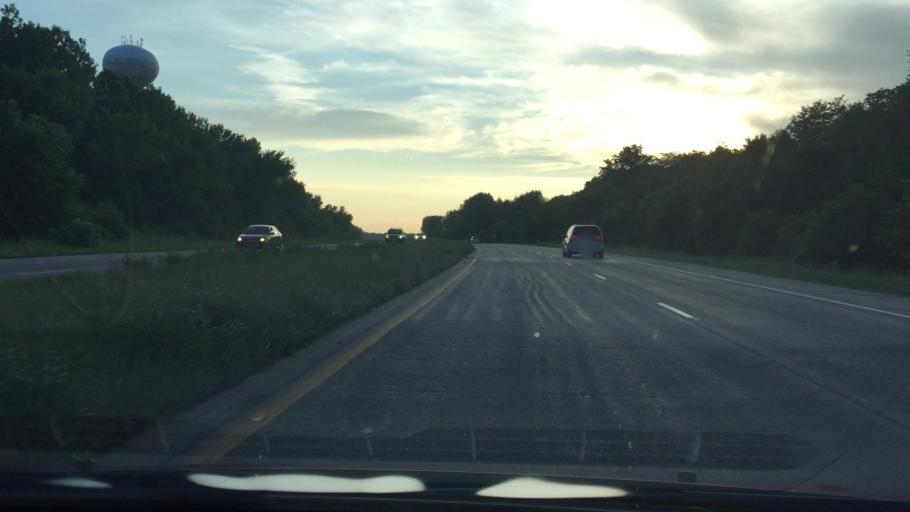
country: US
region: Iowa
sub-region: Muscatine County
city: Muscatine
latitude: 41.4530
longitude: -91.0515
